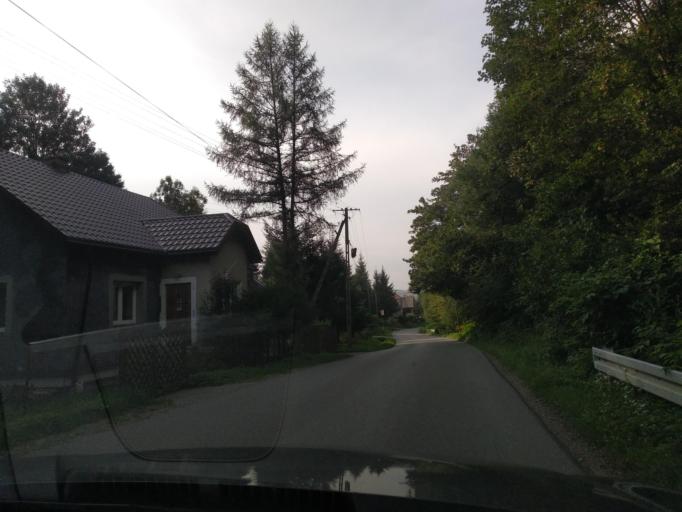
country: PL
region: Subcarpathian Voivodeship
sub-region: Powiat brzozowski
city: Dydnia
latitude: 49.6651
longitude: 22.1934
